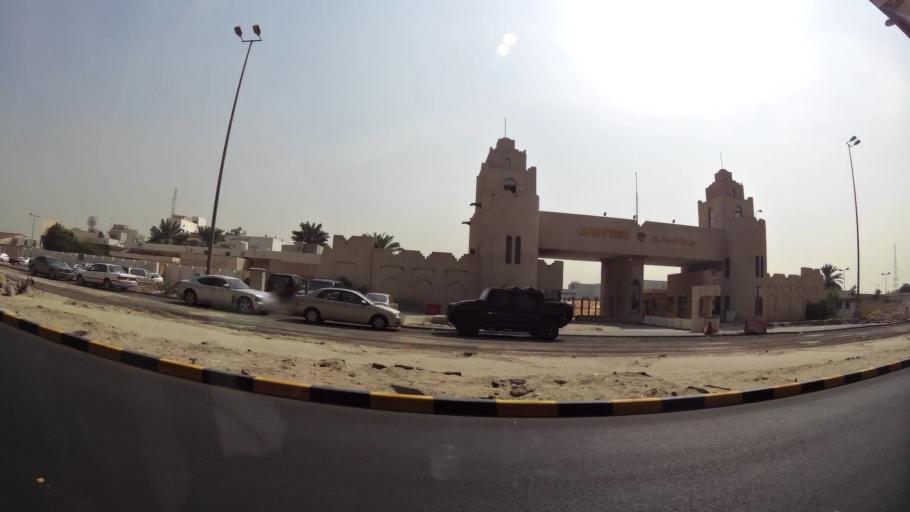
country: KW
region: Al Asimah
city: Ar Rabiyah
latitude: 29.3247
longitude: 47.9157
